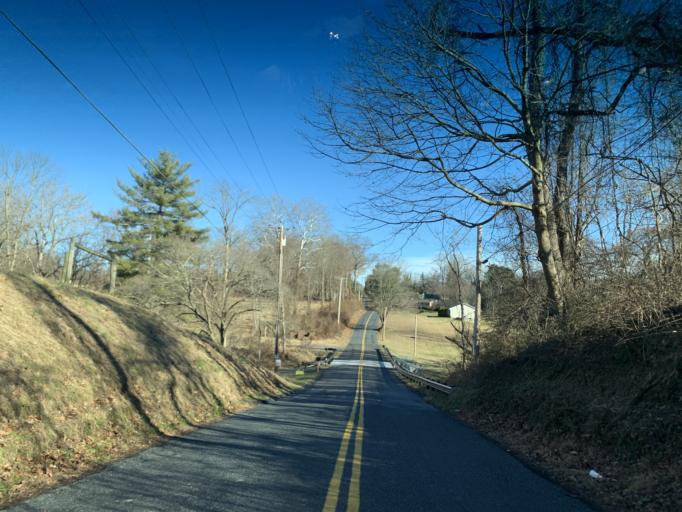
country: US
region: Maryland
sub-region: Harford County
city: Riverside
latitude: 39.5350
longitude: -76.2571
